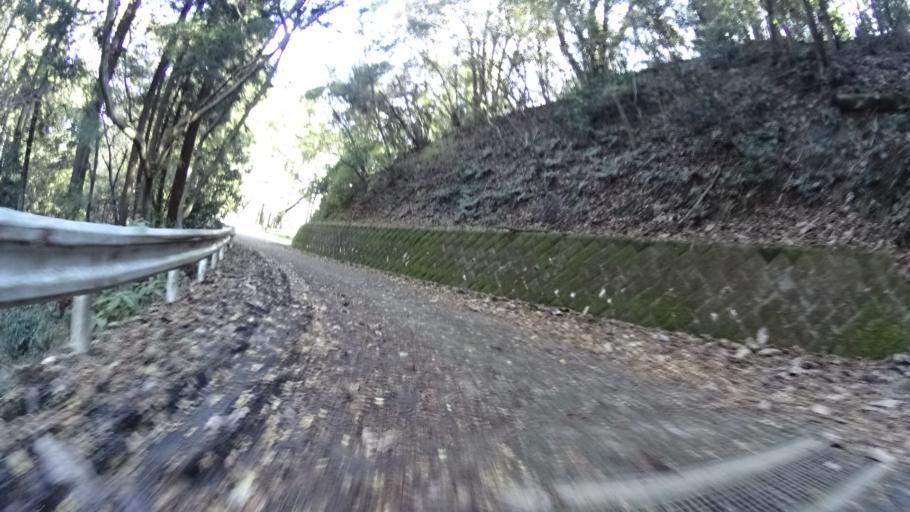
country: JP
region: Kanagawa
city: Zama
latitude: 35.5234
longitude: 139.2742
